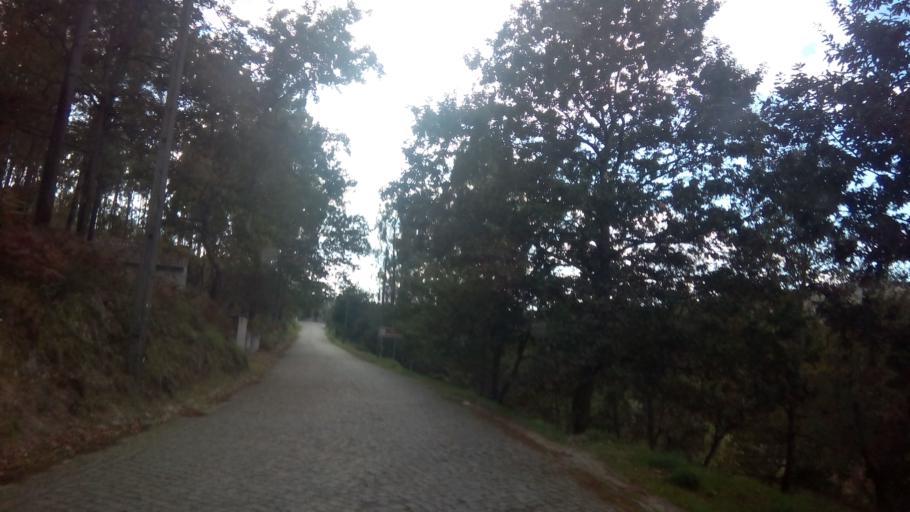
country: PT
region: Porto
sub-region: Amarante
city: Amarante
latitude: 41.2714
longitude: -7.9997
